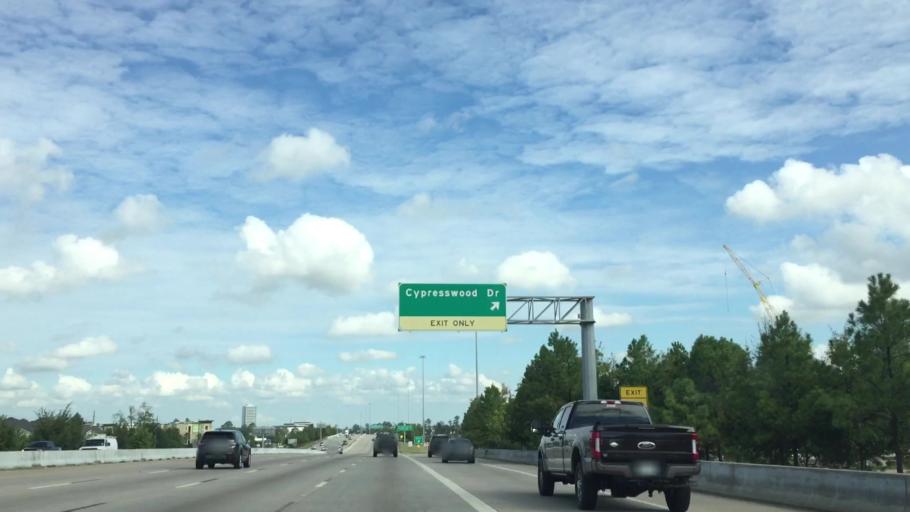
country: US
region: Texas
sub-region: Harris County
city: Oak Cliff Place
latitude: 29.9747
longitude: -95.5639
